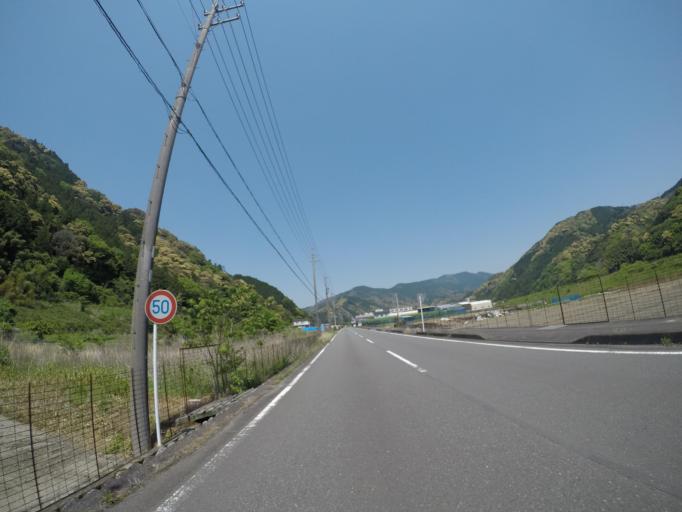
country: JP
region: Shizuoka
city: Shizuoka-shi
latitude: 34.9986
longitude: 138.2845
